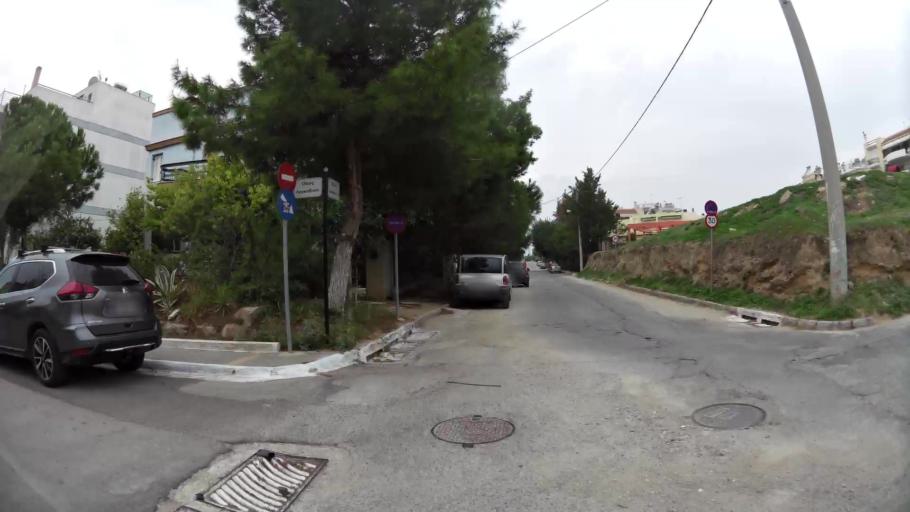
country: GR
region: Attica
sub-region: Nomarchia Athinas
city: Alimos
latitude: 37.9174
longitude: 23.7269
